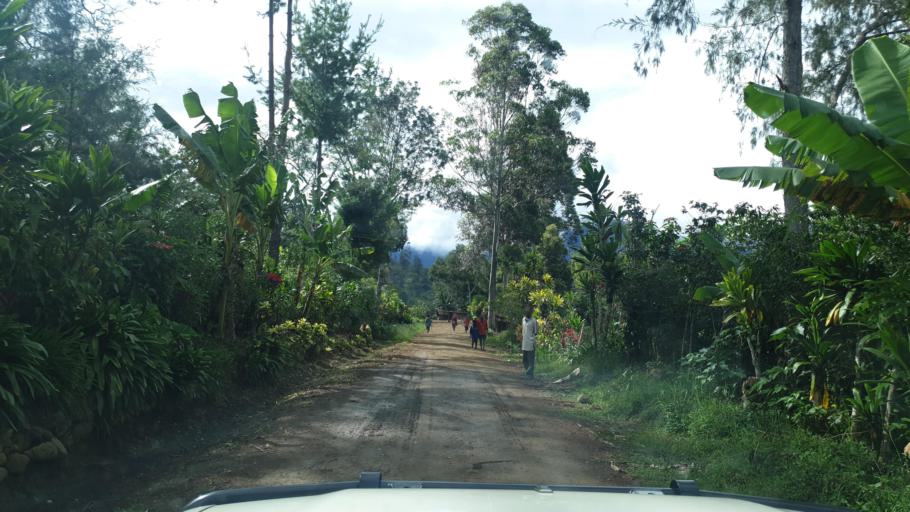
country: PG
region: Eastern Highlands
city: Goroka
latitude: -5.9385
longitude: 145.2680
